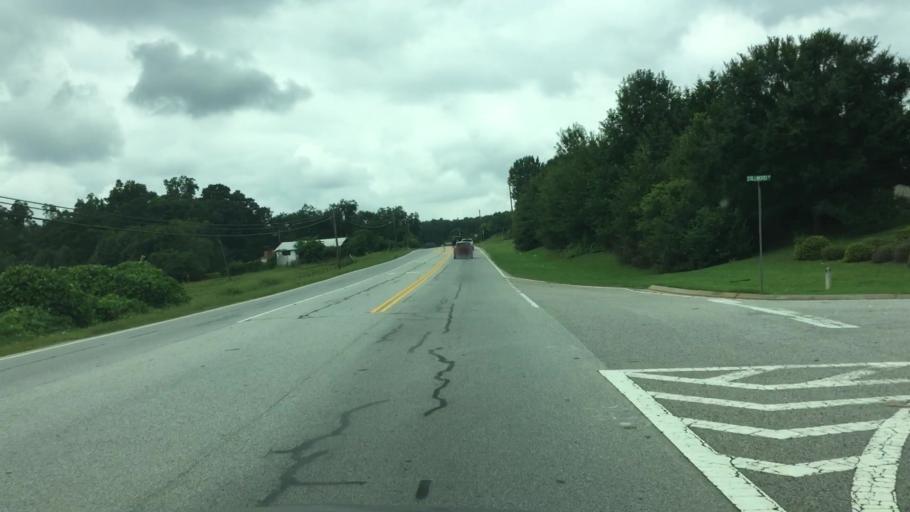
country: US
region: Georgia
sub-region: Barrow County
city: Winder
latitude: 34.0099
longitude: -83.7566
